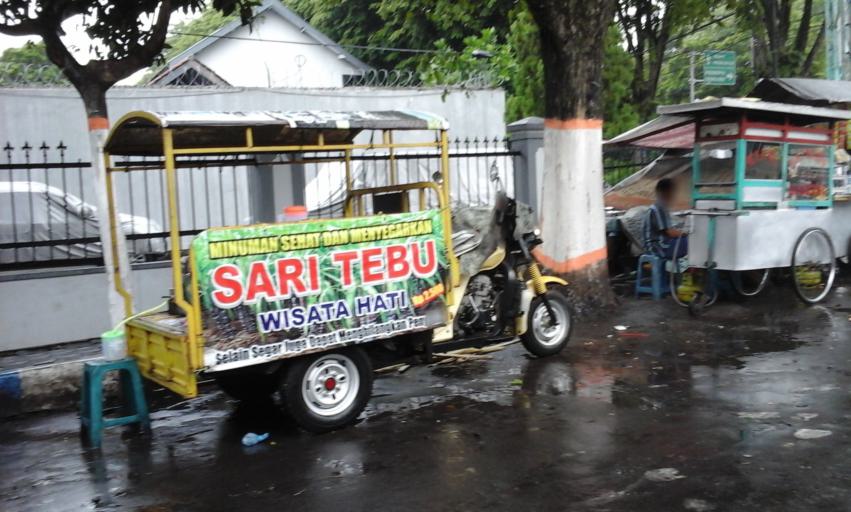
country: ID
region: East Java
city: Lumajang
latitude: -8.1357
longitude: 113.2256
